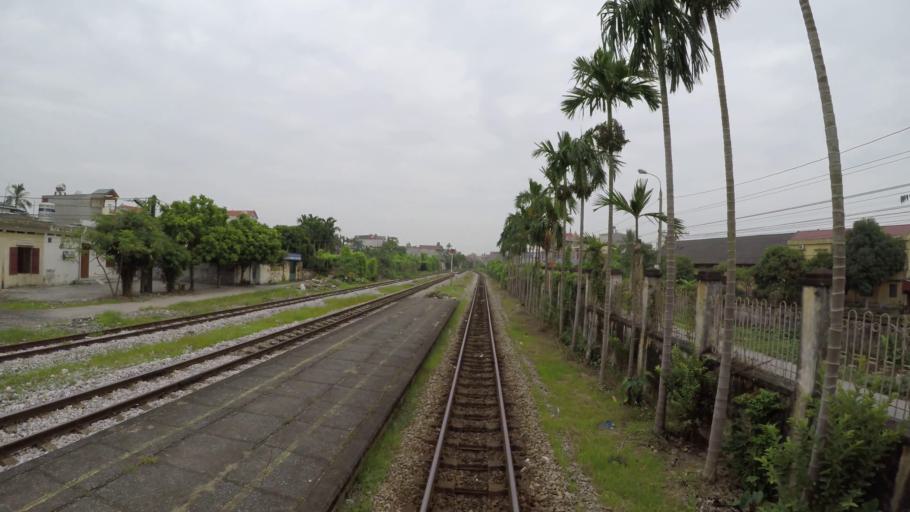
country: VN
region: Hai Duong
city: Phu Thai
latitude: 20.9728
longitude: 106.4881
